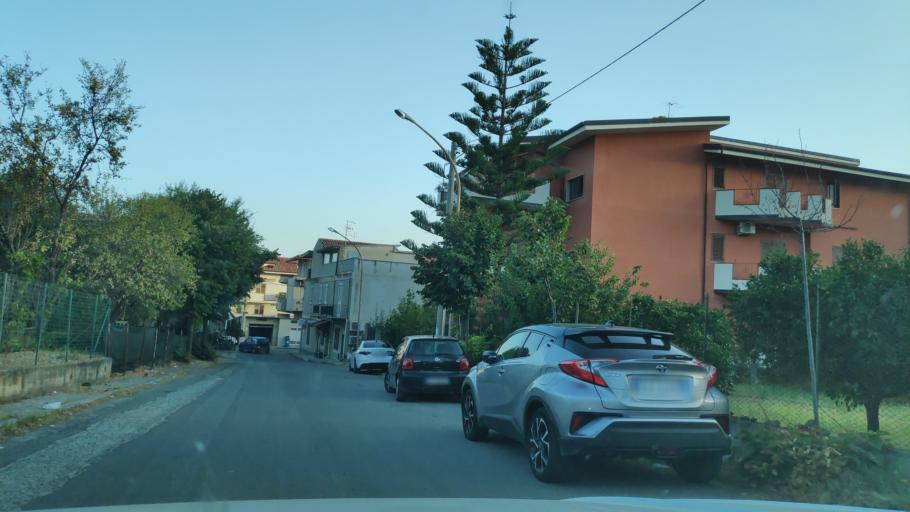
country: IT
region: Calabria
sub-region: Provincia di Reggio Calabria
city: Bova Marina
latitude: 37.9301
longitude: 15.9112
